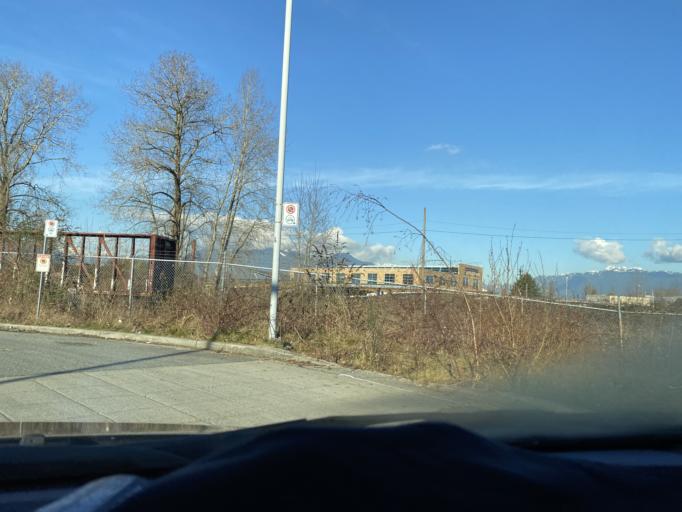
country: CA
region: British Columbia
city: Vancouver
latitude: 49.2671
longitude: -123.0864
